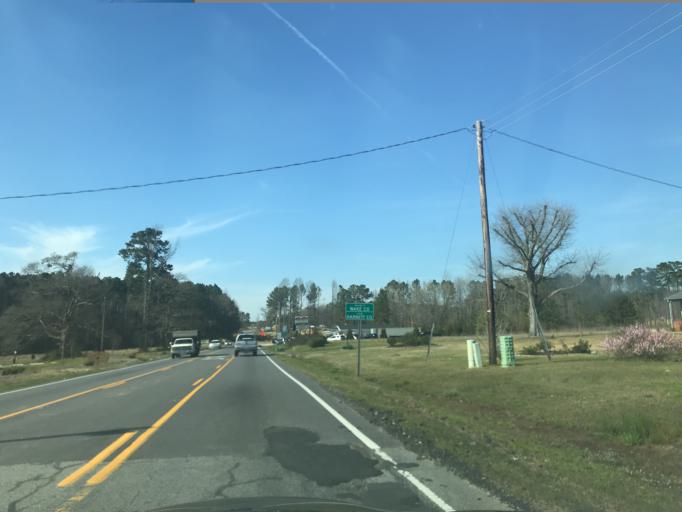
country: US
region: North Carolina
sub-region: Harnett County
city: Angier
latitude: 35.5298
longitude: -78.7443
